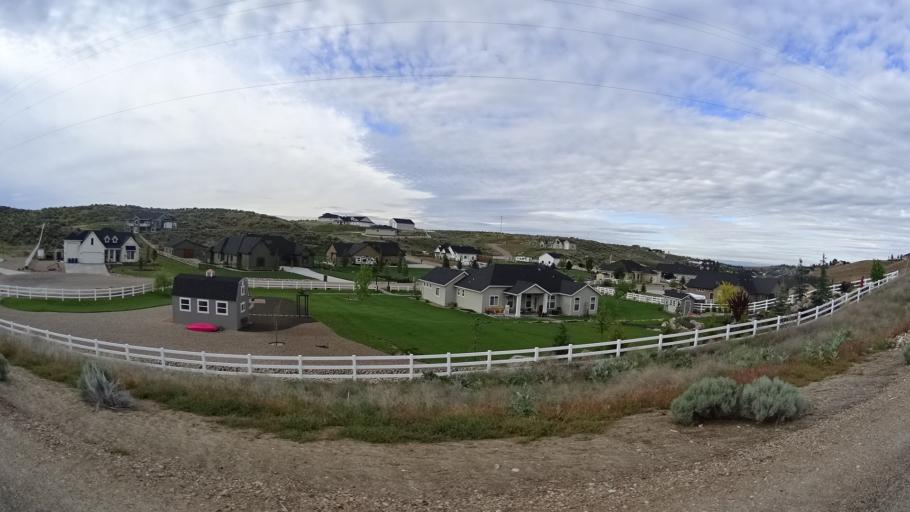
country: US
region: Idaho
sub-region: Ada County
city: Star
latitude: 43.7359
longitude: -116.5247
